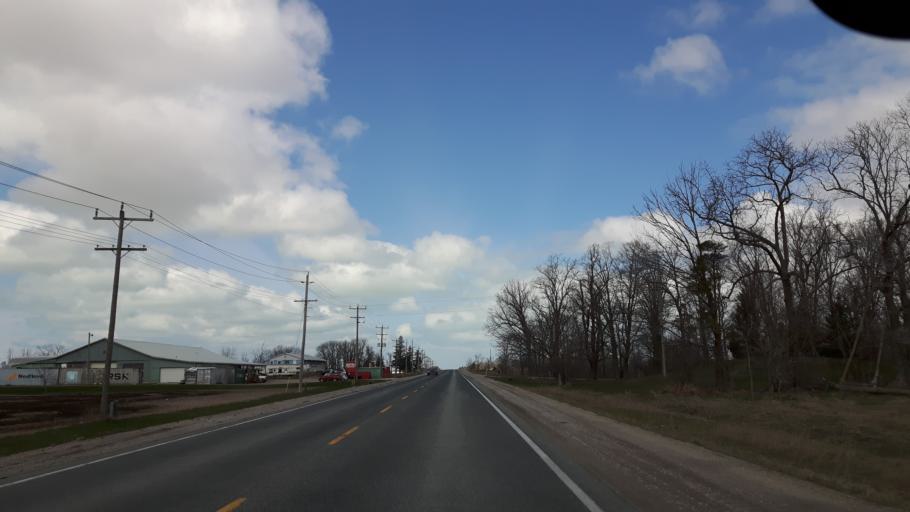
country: CA
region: Ontario
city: Goderich
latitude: 43.7171
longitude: -81.6701
